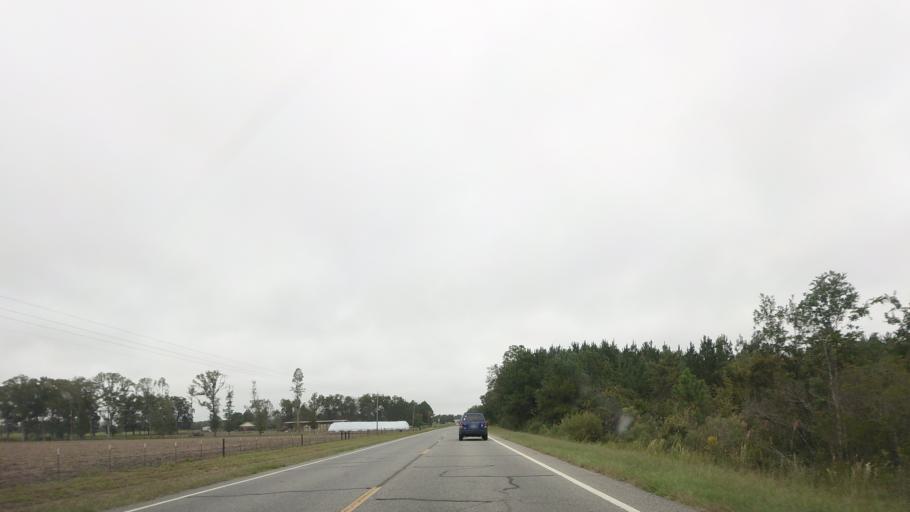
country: US
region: Georgia
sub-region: Irwin County
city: Ocilla
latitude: 31.5697
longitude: -83.2530
